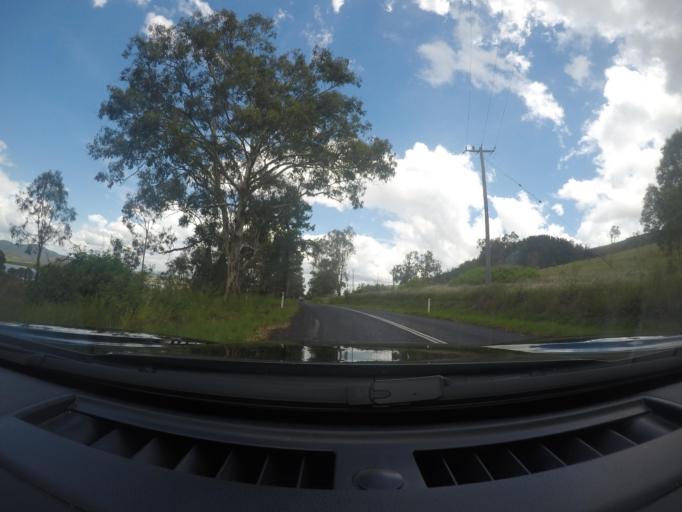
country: AU
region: Queensland
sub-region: Moreton Bay
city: Woodford
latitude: -27.0831
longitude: 152.5613
